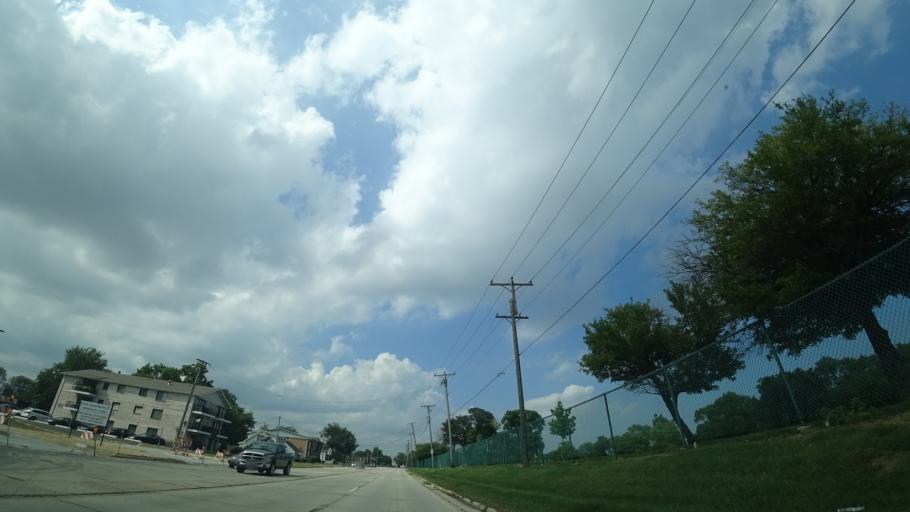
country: US
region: Illinois
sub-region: Cook County
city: Chicago Ridge
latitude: 41.6876
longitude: -87.7786
